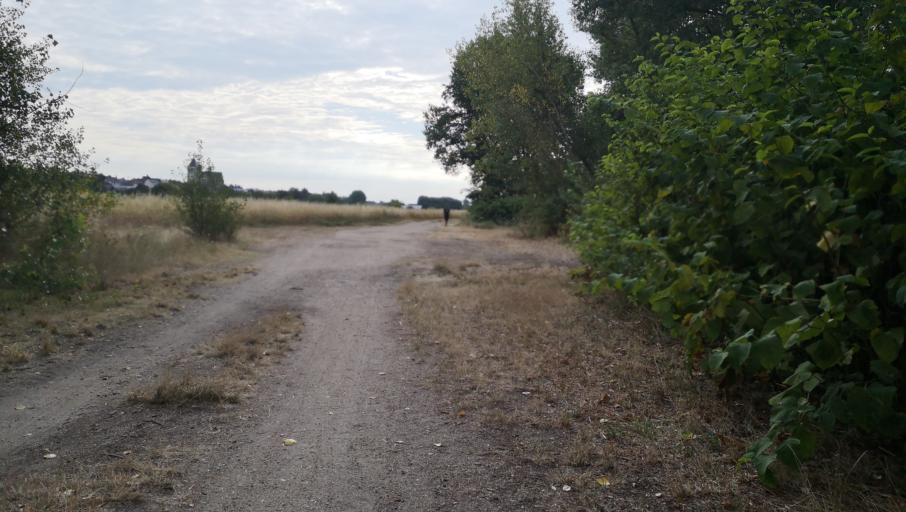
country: FR
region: Centre
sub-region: Departement du Loiret
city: Checy
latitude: 47.8890
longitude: 2.0149
